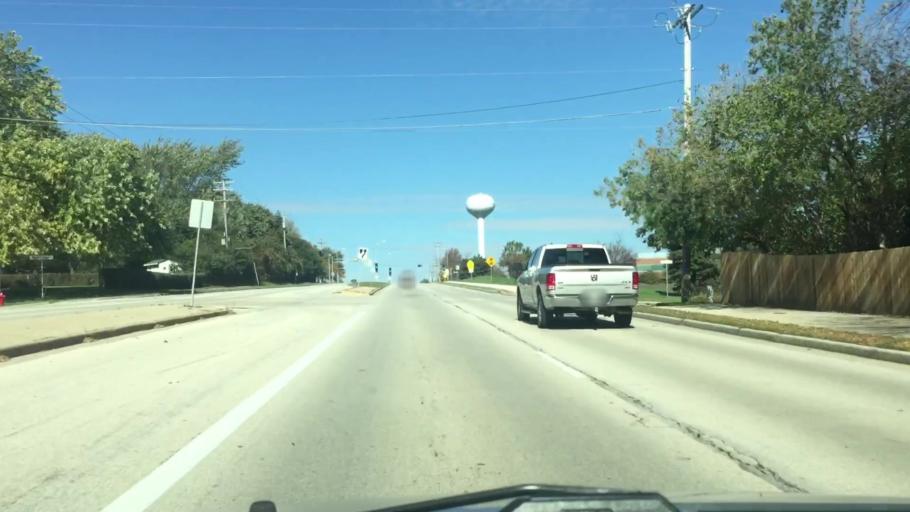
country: US
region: Wisconsin
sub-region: Waukesha County
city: Waukesha
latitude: 43.0282
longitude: -88.1668
